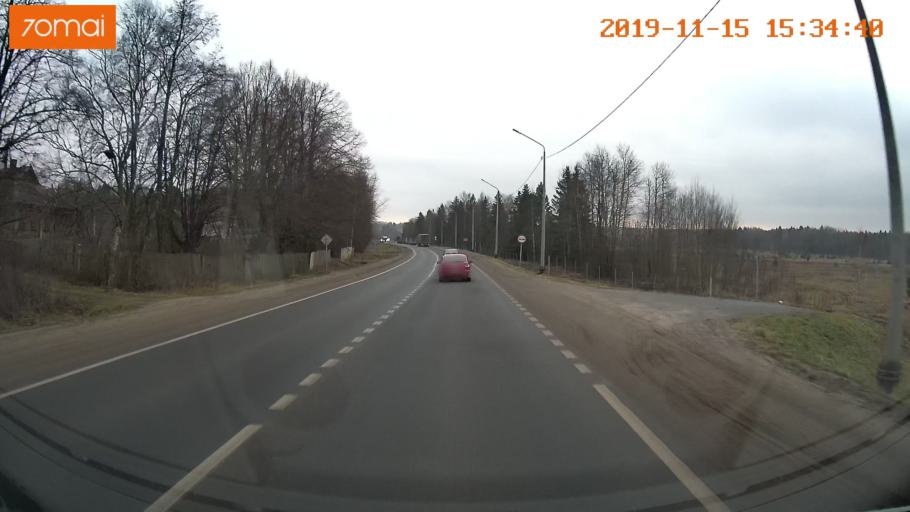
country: RU
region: Jaroslavl
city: Danilov
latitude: 58.0670
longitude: 40.0883
